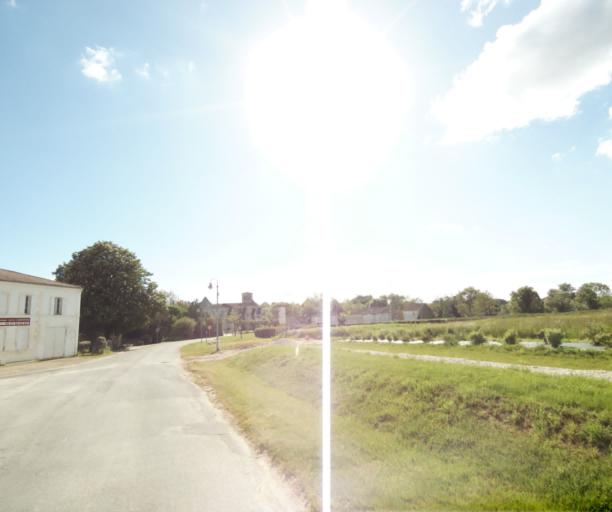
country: FR
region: Poitou-Charentes
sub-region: Departement de la Charente-Maritime
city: Nieul-les-Saintes
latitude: 45.7062
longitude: -0.7332
